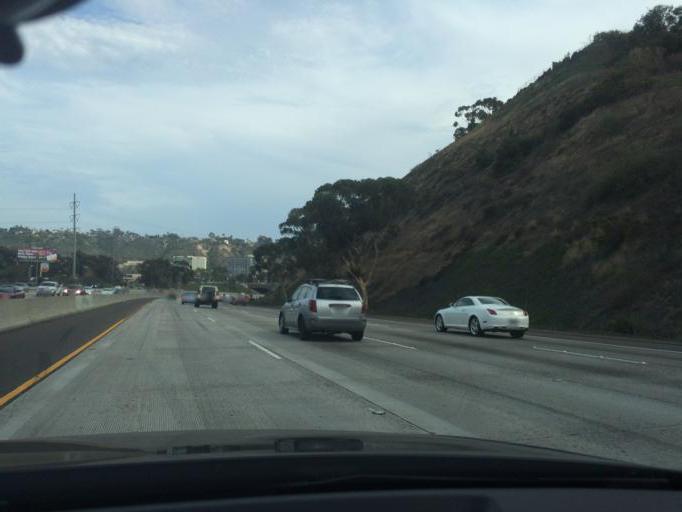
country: US
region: California
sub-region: San Diego County
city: San Diego
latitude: 32.7763
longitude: -117.1622
